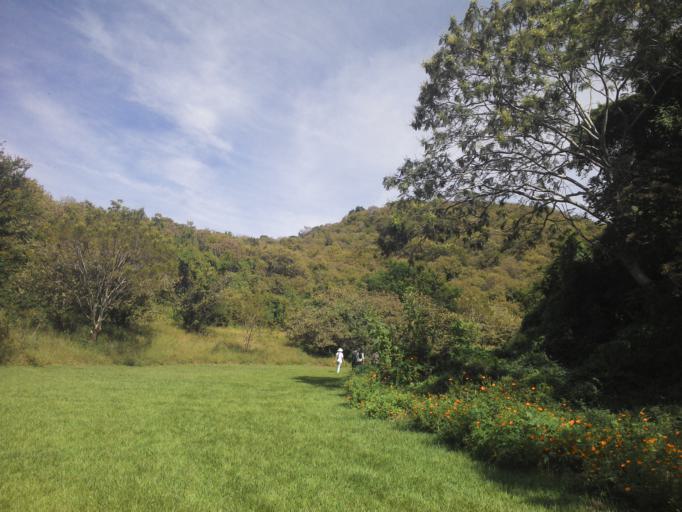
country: MX
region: Jalisco
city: Teuchitlan
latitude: 20.6957
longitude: -103.8355
